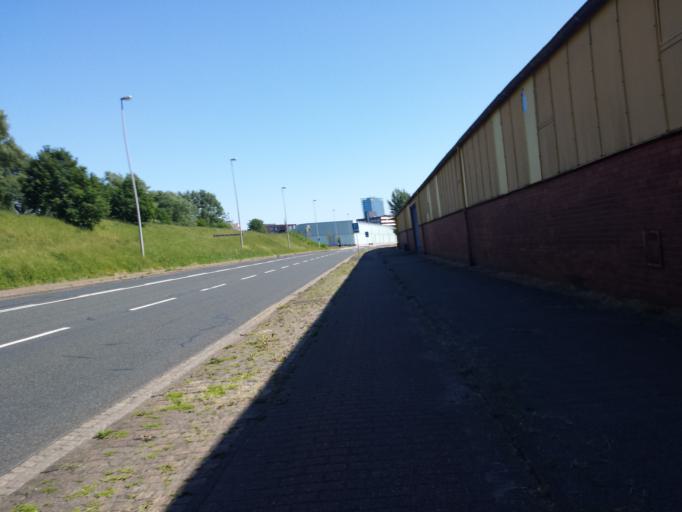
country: DE
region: Bremen
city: Bremen
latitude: 53.0917
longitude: 8.7801
